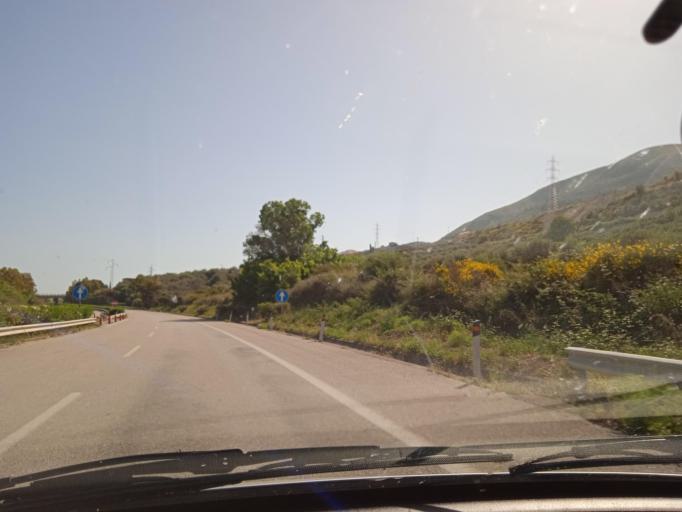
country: IT
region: Sicily
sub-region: Messina
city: Torrenova
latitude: 38.0863
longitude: 14.6911
